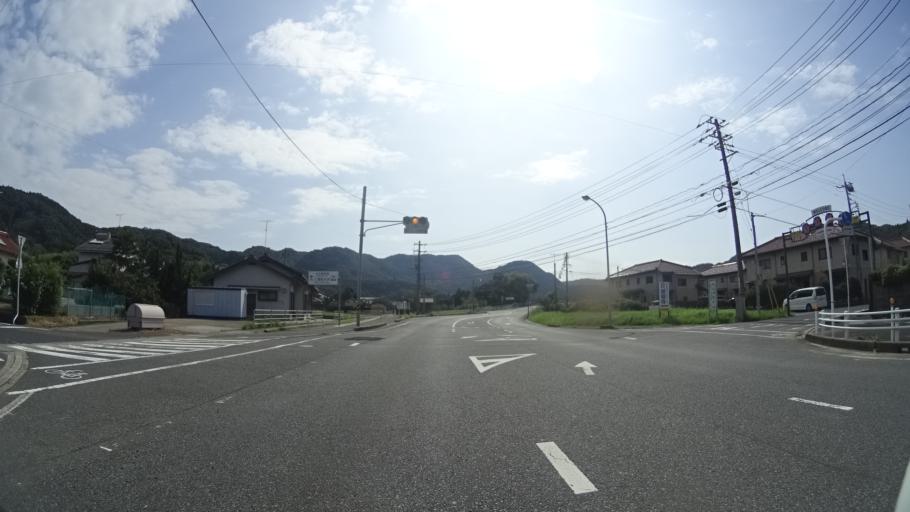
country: JP
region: Shimane
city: Odacho-oda
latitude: 35.1474
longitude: 132.4088
